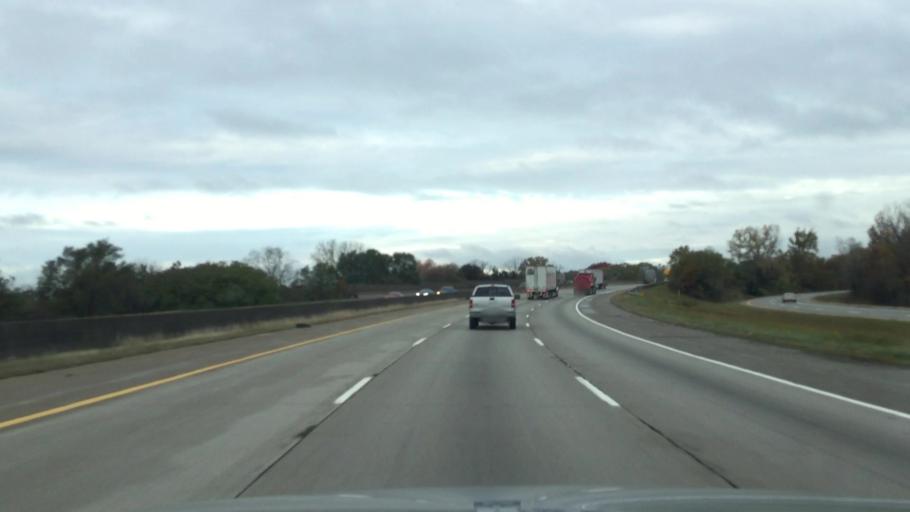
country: US
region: Michigan
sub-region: Washtenaw County
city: Ypsilanti
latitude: 42.2183
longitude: -83.5591
